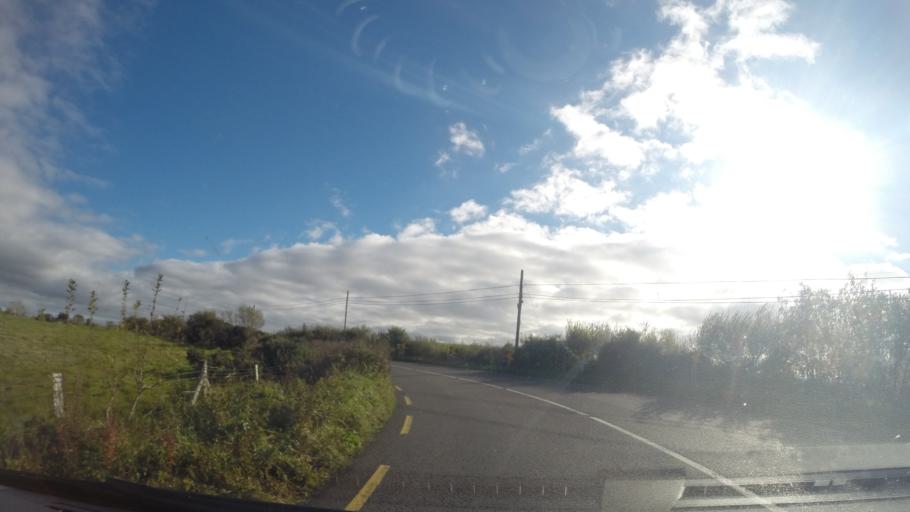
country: IE
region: Ulster
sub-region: County Donegal
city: Killybegs
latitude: 54.6332
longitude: -8.3843
